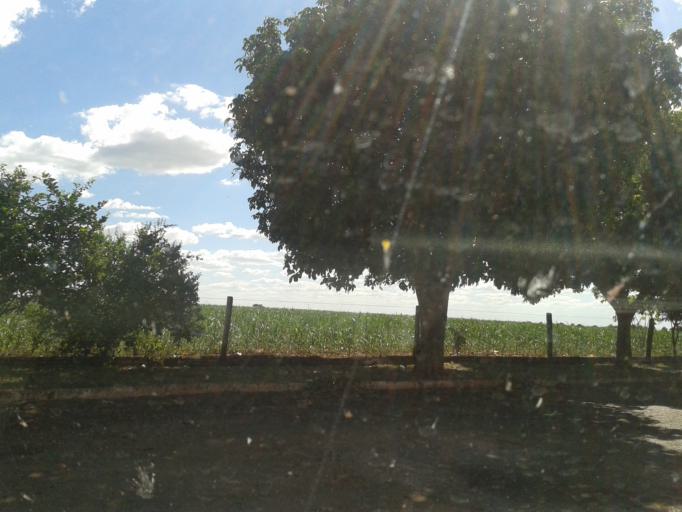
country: BR
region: Minas Gerais
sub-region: Santa Vitoria
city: Santa Vitoria
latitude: -18.6957
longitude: -49.9486
